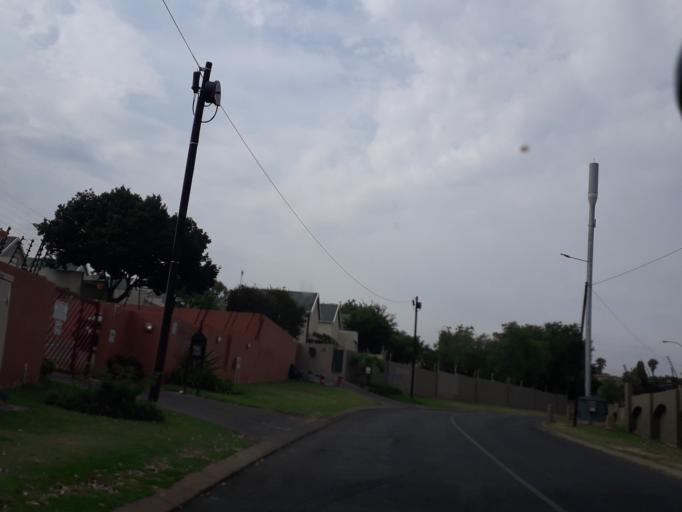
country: ZA
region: Gauteng
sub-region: City of Johannesburg Metropolitan Municipality
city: Roodepoort
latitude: -26.1018
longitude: 27.9217
